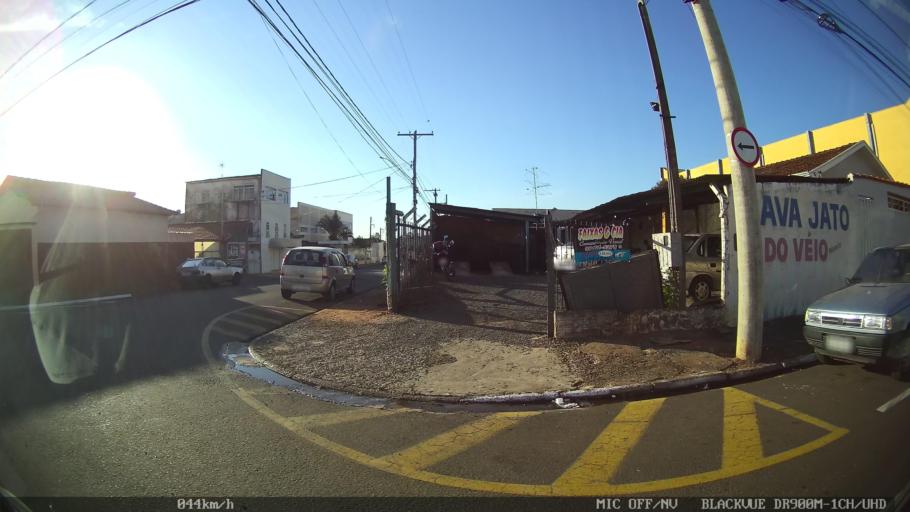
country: BR
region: Sao Paulo
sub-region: Franca
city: Franca
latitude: -20.5251
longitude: -47.3753
